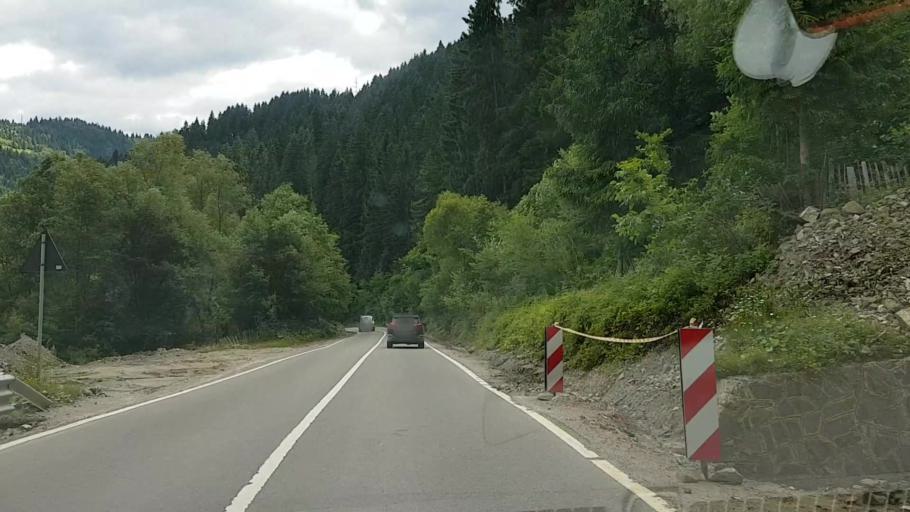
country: RO
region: Neamt
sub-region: Comuna Farcasa
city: Farcasa
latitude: 47.1401
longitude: 25.8595
